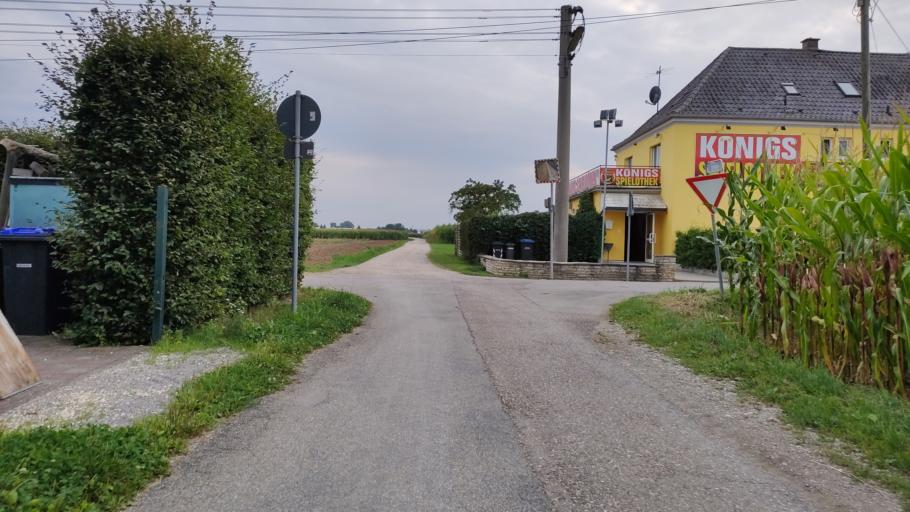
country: DE
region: Bavaria
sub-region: Swabia
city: Konigsbrunn
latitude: 48.2623
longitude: 10.8799
